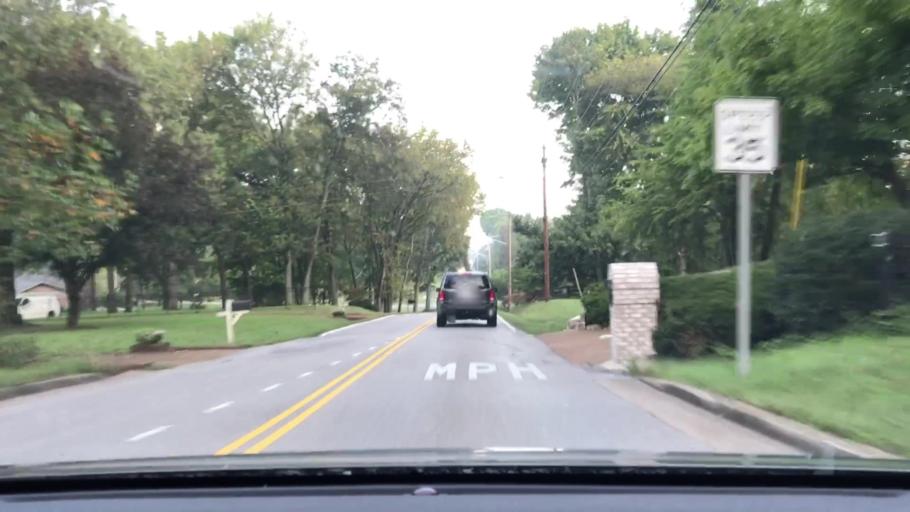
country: US
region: Tennessee
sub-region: Williamson County
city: Brentwood Estates
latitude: 36.0338
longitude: -86.7688
